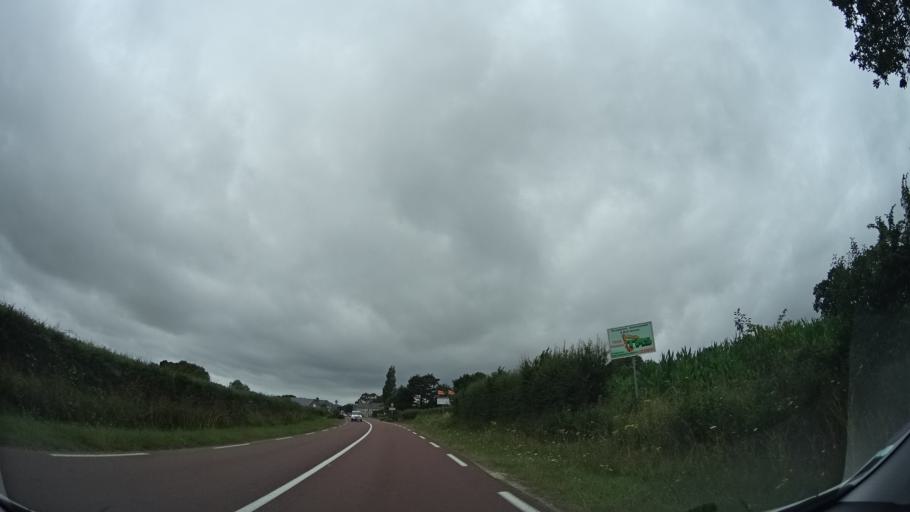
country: FR
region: Lower Normandy
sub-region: Departement de la Manche
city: La Haye-du-Puits
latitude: 49.2998
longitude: -1.5695
